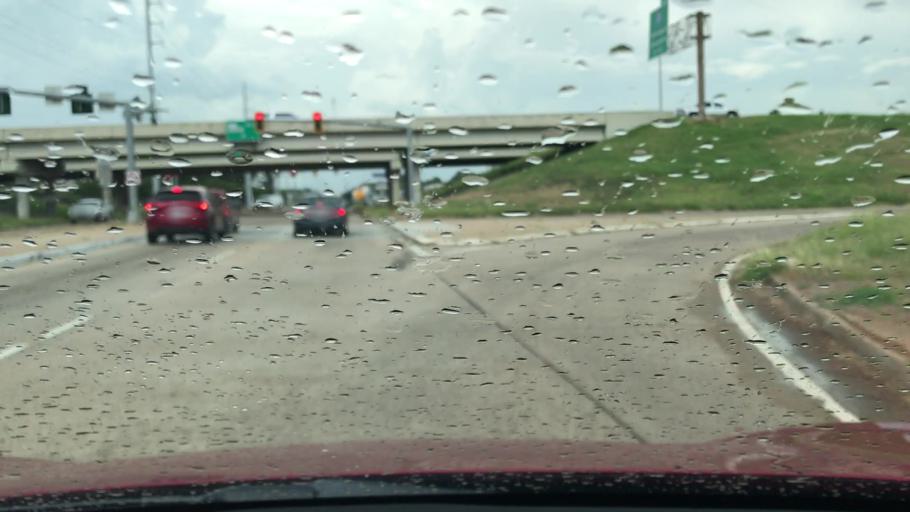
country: US
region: Louisiana
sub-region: Bossier Parish
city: Bossier City
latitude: 32.4196
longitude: -93.7630
